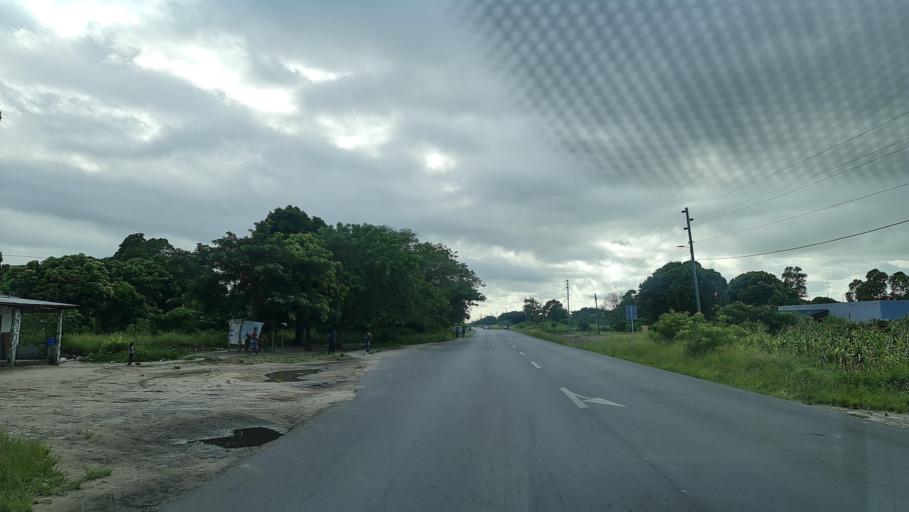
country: MZ
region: Maputo
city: Manhica
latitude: -25.4106
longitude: 32.7484
